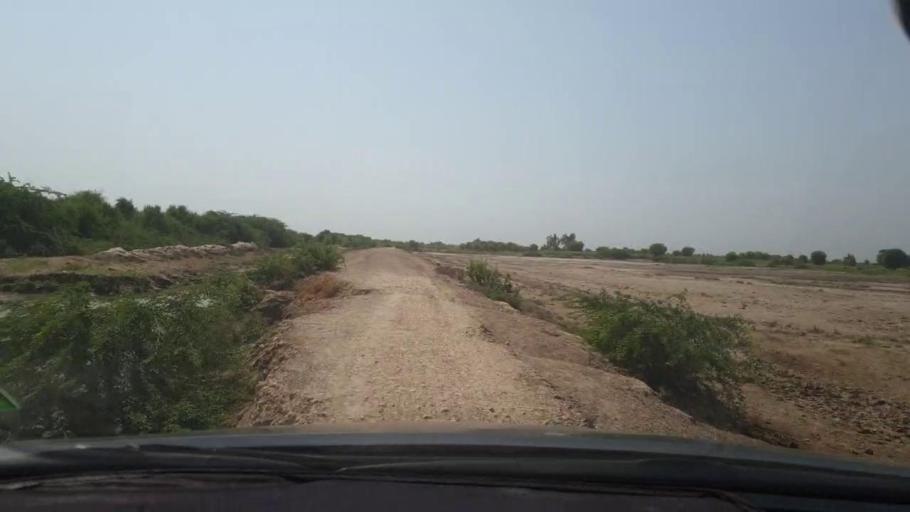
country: PK
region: Sindh
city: Tando Bago
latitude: 24.7938
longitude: 69.1793
